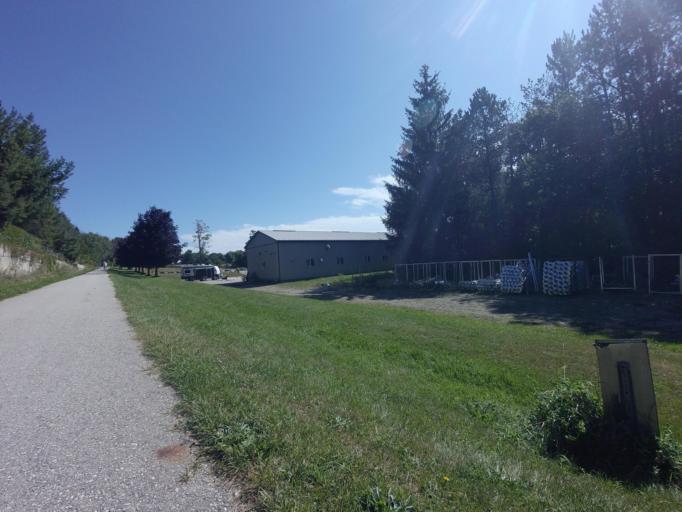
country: CA
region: Ontario
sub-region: Wellington County
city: Guelph
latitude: 43.6921
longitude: -80.4162
